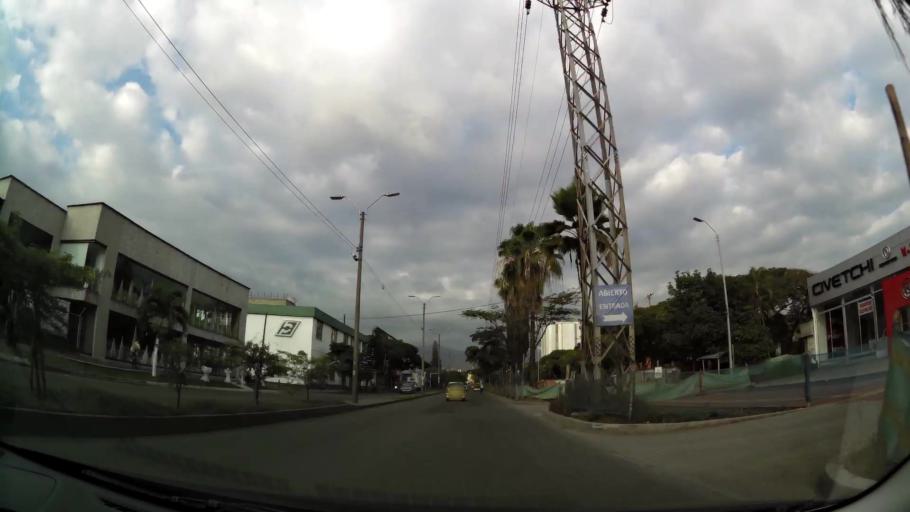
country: CO
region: Valle del Cauca
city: Cali
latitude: 3.4540
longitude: -76.5137
